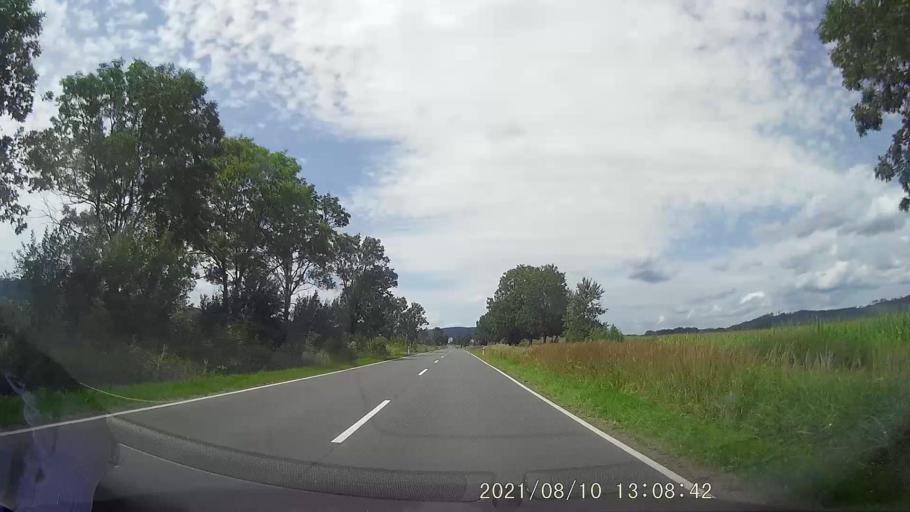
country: PL
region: Lower Silesian Voivodeship
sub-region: Powiat klodzki
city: Bozkow
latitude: 50.4943
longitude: 16.5530
